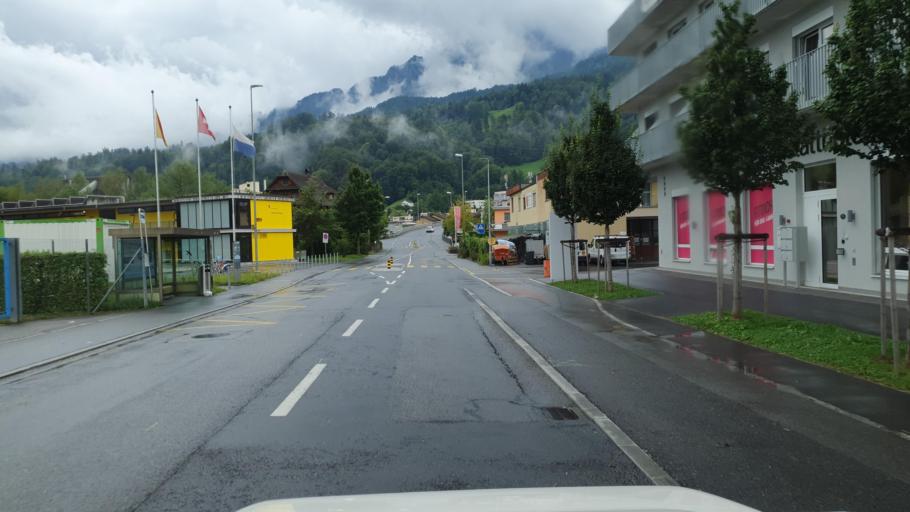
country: CH
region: Lucerne
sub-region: Lucerne-Land District
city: Horw
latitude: 47.0125
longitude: 8.3090
